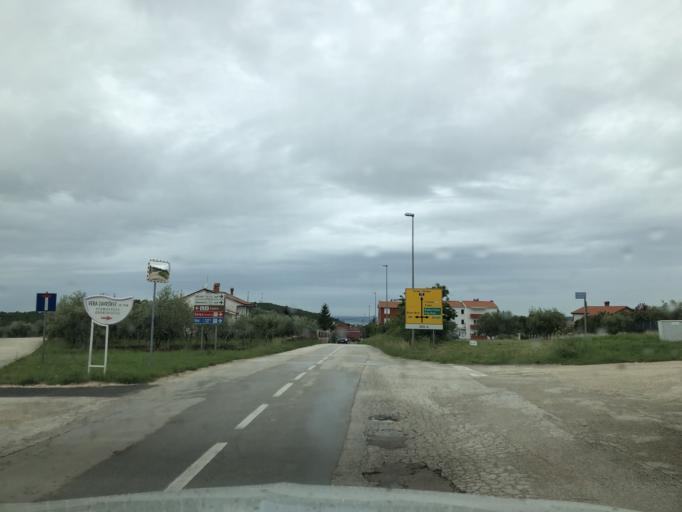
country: HR
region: Istarska
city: Buje
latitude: 45.4485
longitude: 13.6388
